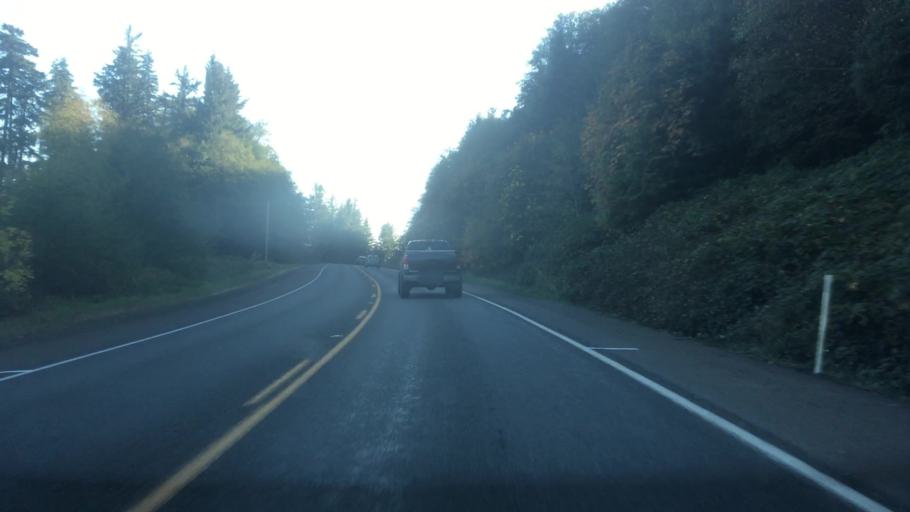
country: US
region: Oregon
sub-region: Clatsop County
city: Astoria
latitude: 46.2581
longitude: -123.8531
